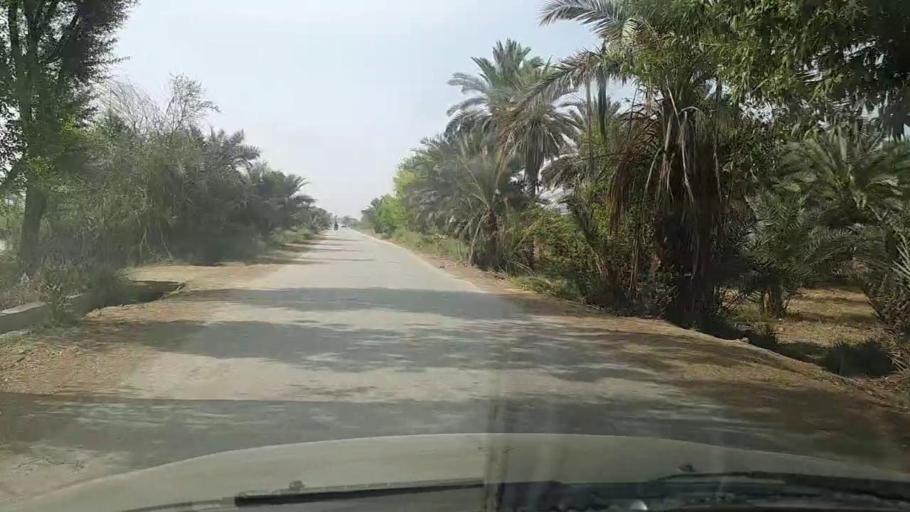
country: PK
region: Sindh
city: Gambat
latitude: 27.4503
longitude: 68.4861
